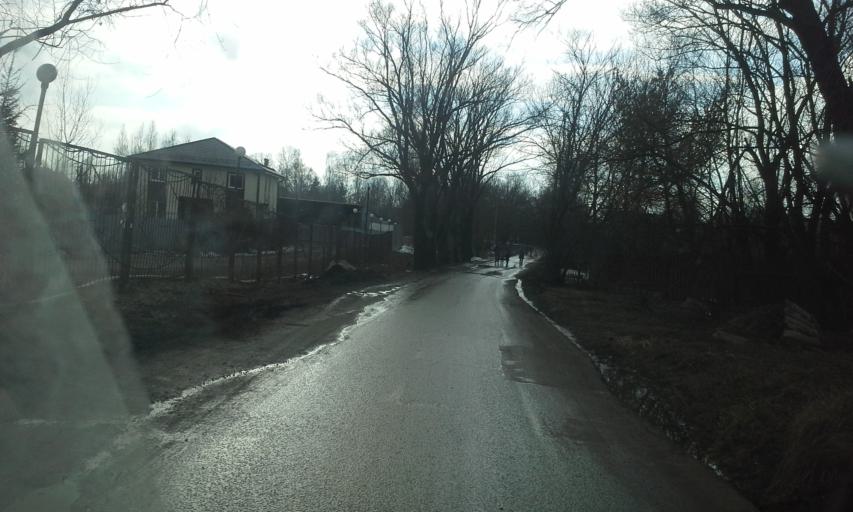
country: RU
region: Moscow
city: Tolstopal'tsevo
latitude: 55.6087
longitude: 37.2158
